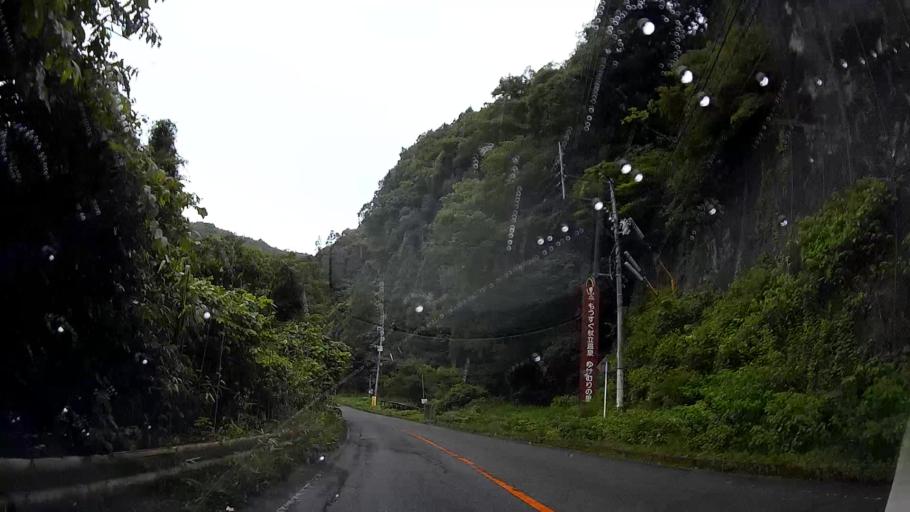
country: JP
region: Oita
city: Tsukawaki
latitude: 33.1686
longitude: 131.0417
